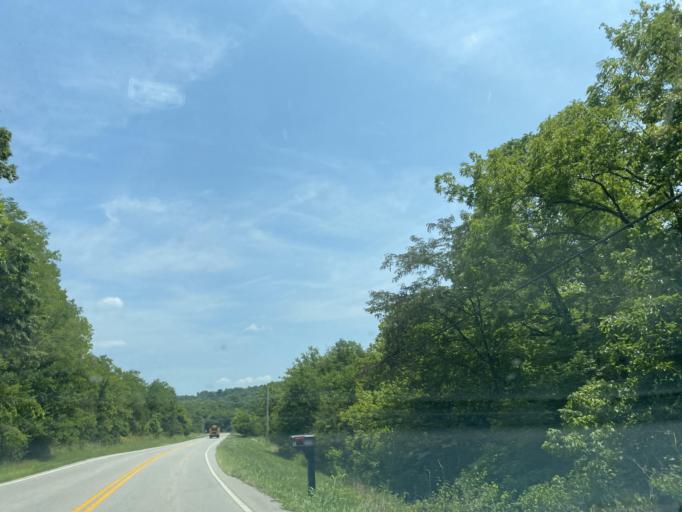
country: US
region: Kentucky
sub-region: Campbell County
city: Claryville
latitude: 38.9276
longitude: -84.4318
